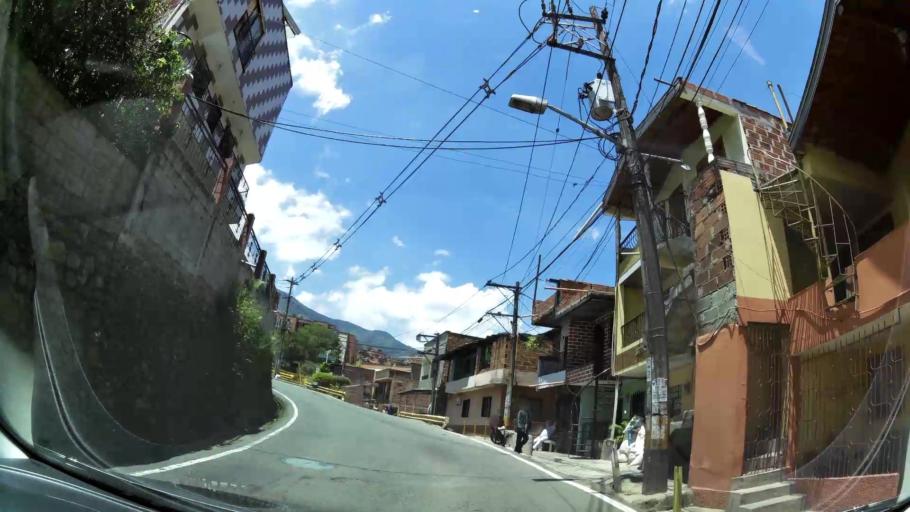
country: CO
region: Antioquia
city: La Estrella
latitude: 6.1868
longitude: -75.6465
